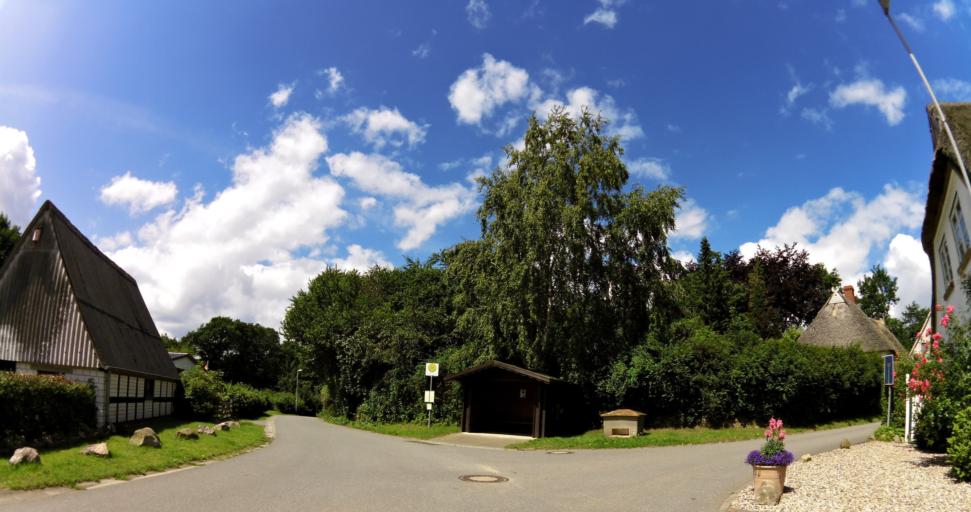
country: DE
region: Schleswig-Holstein
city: Brodersby
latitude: 54.5224
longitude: 9.7201
